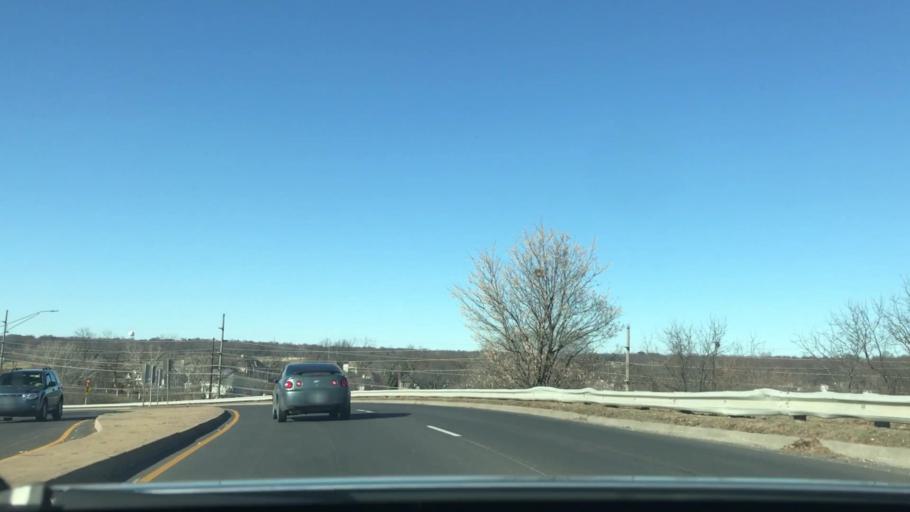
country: US
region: Missouri
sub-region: Jackson County
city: Independence
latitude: 39.0555
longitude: -94.3876
